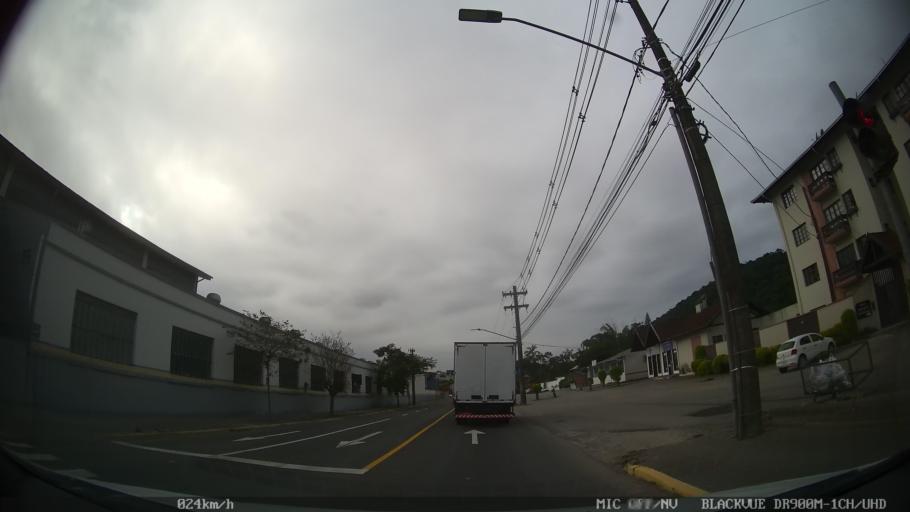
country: BR
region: Santa Catarina
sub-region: Joinville
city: Joinville
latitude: -26.2926
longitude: -48.8645
